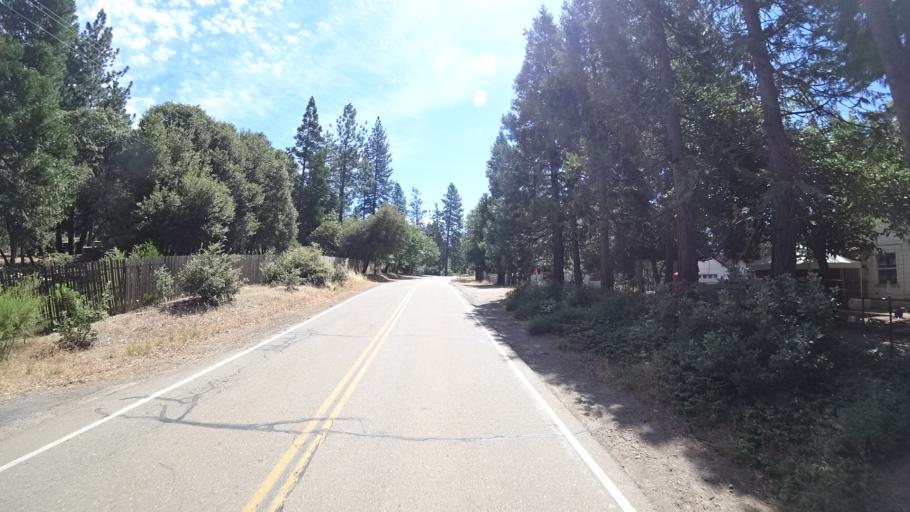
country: US
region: California
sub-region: Amador County
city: Pioneer
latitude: 38.3359
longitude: -120.5349
